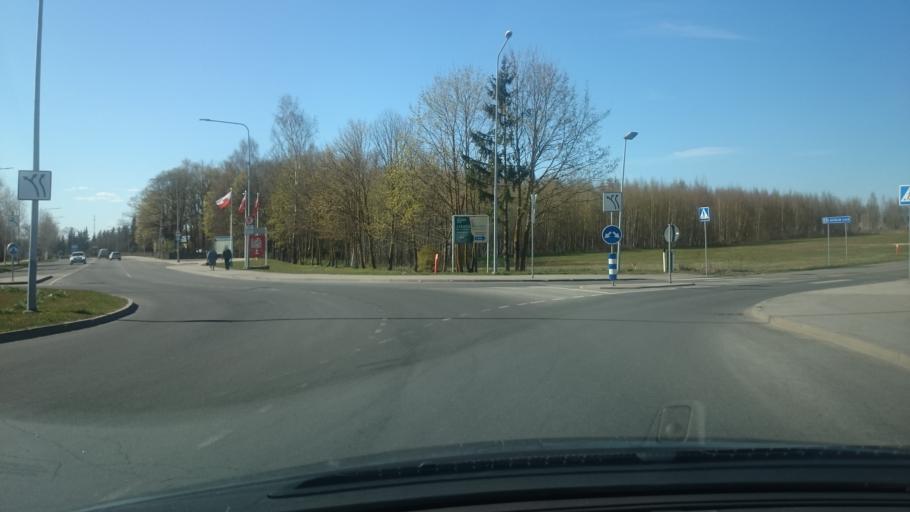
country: EE
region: Tartu
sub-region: Tartu linn
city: Tartu
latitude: 58.3780
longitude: 26.7775
